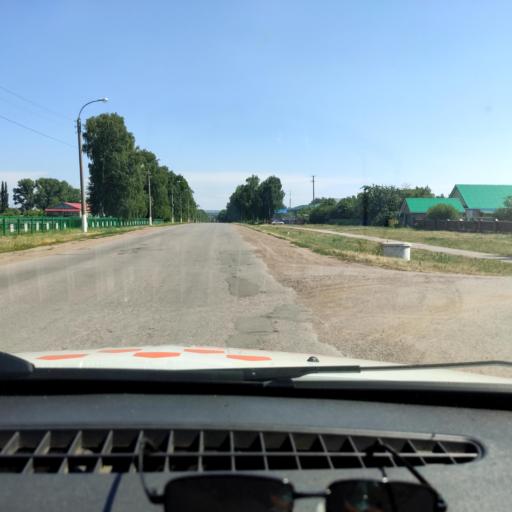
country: RU
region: Bashkortostan
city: Tolbazy
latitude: 54.0097
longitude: 55.8880
